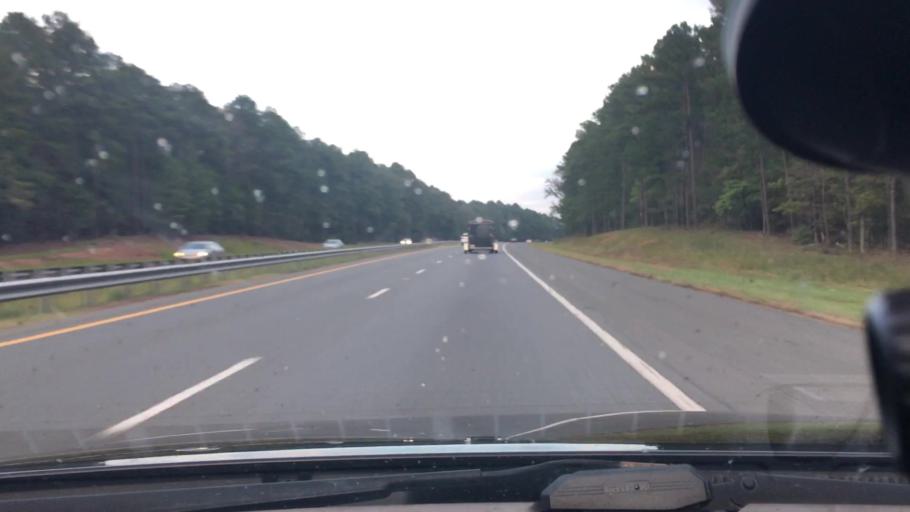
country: US
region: North Carolina
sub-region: Chatham County
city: Pittsboro
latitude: 35.6427
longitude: -79.0240
